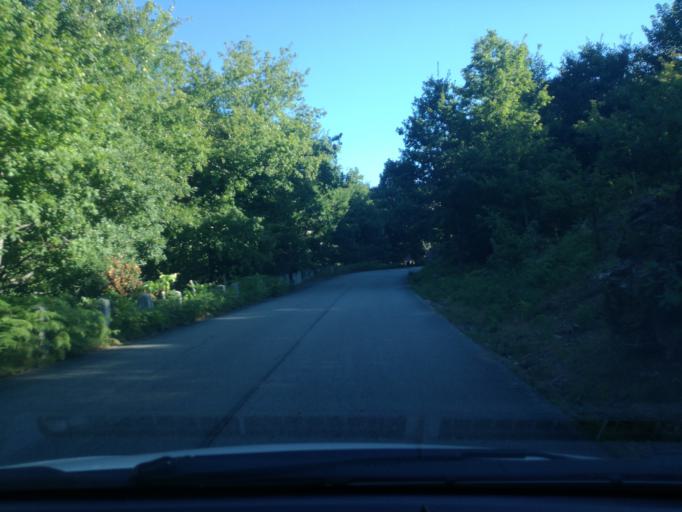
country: PT
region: Braga
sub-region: Vieira do Minho
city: Real
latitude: 41.7461
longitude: -8.1550
